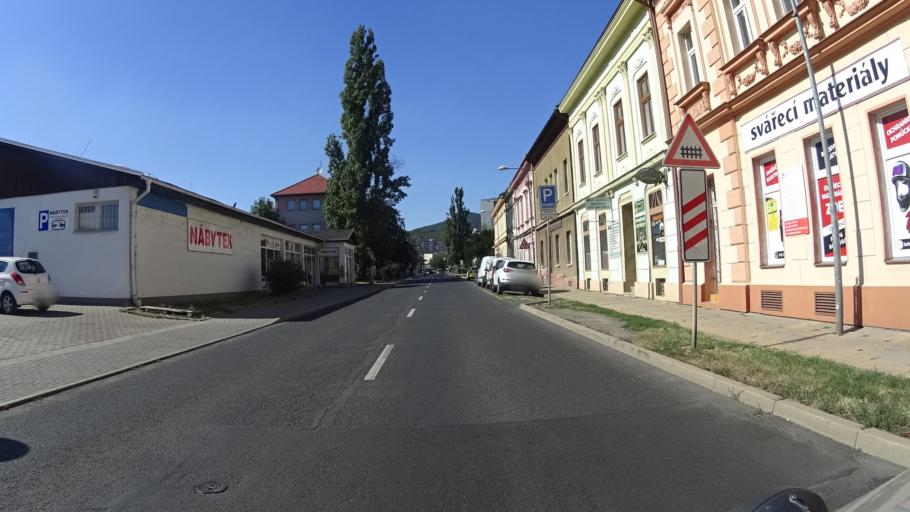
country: CZ
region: Ustecky
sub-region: Okres Litomerice
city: Litomerice
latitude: 50.5398
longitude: 14.1262
